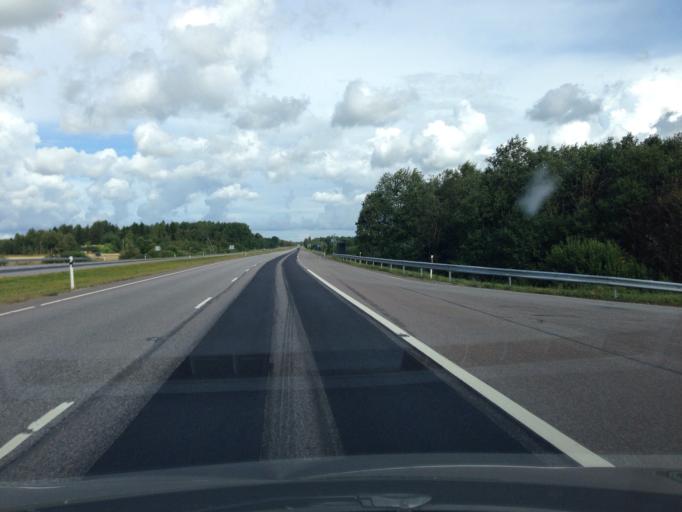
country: EE
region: Harju
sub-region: Saue linn
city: Saue
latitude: 59.2774
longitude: 24.5253
